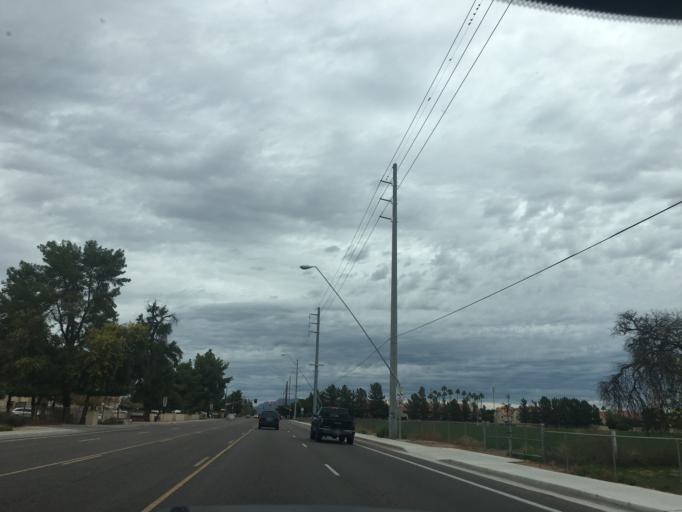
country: US
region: Arizona
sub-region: Maricopa County
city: Mesa
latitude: 33.4326
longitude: -111.8313
